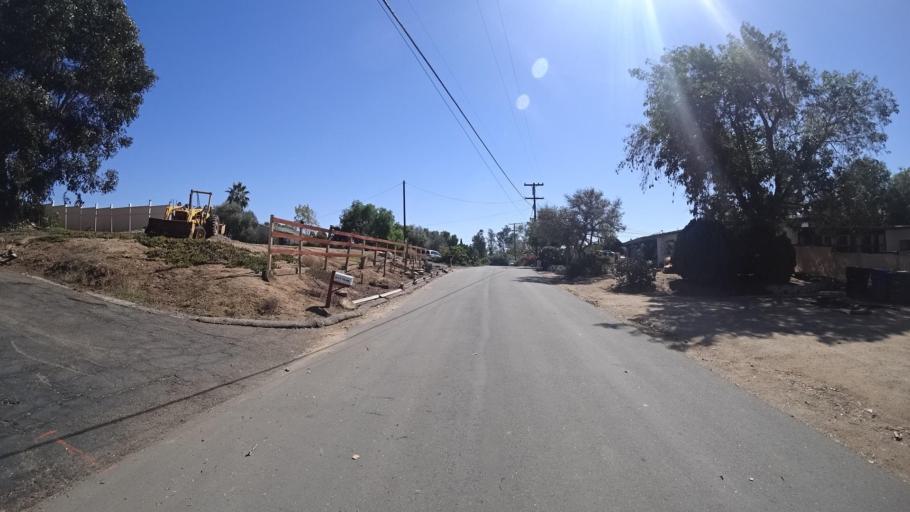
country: US
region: California
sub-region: San Diego County
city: Bonita
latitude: 32.6654
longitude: -117.0458
